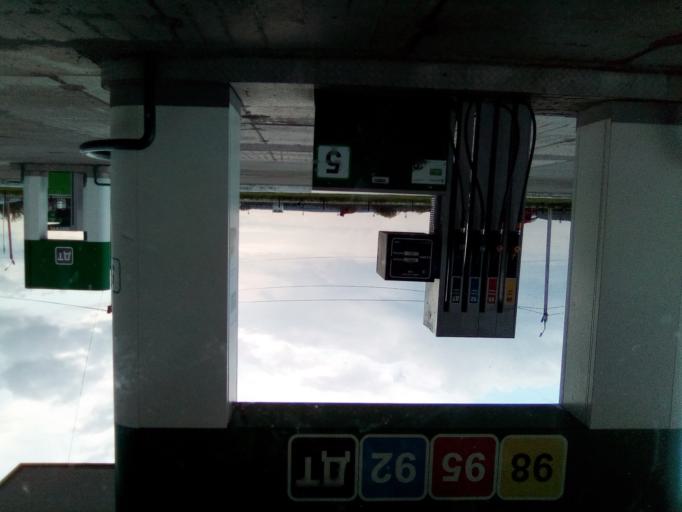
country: RU
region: Chelyabinsk
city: Poletayevo
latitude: 54.9894
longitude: 61.0432
